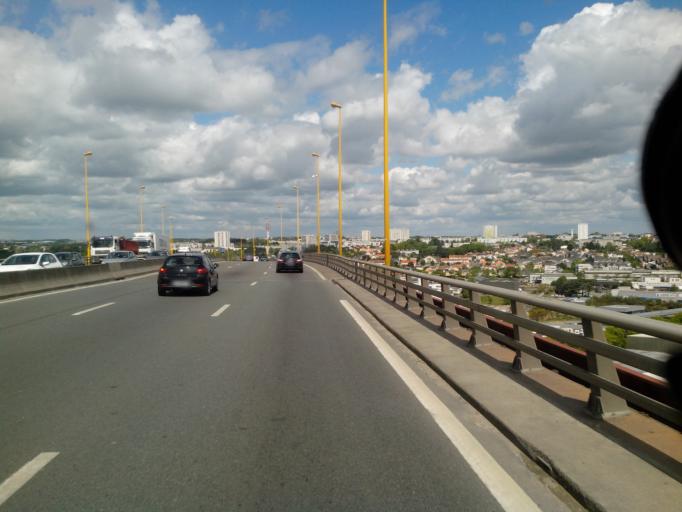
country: FR
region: Pays de la Loire
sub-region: Departement de la Loire-Atlantique
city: Bouguenais
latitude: 47.1934
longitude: -1.6134
